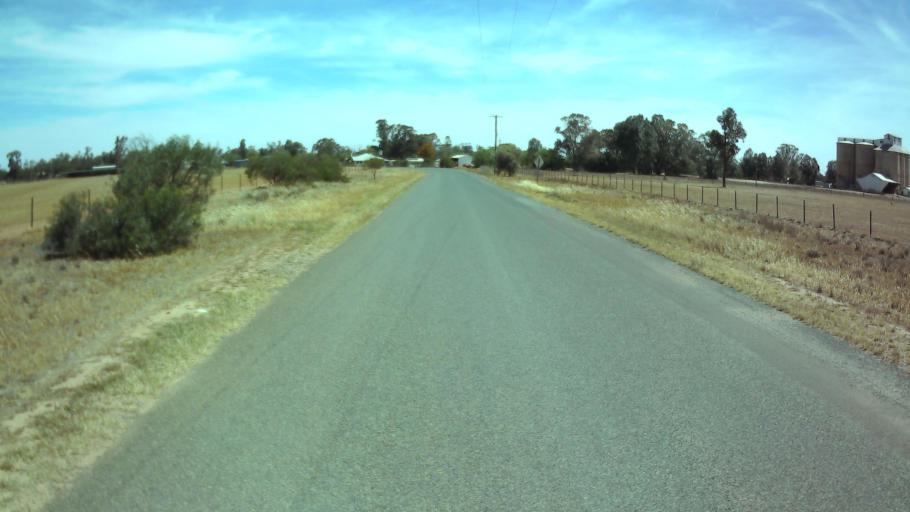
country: AU
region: New South Wales
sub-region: Weddin
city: Grenfell
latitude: -33.8377
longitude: 147.7459
